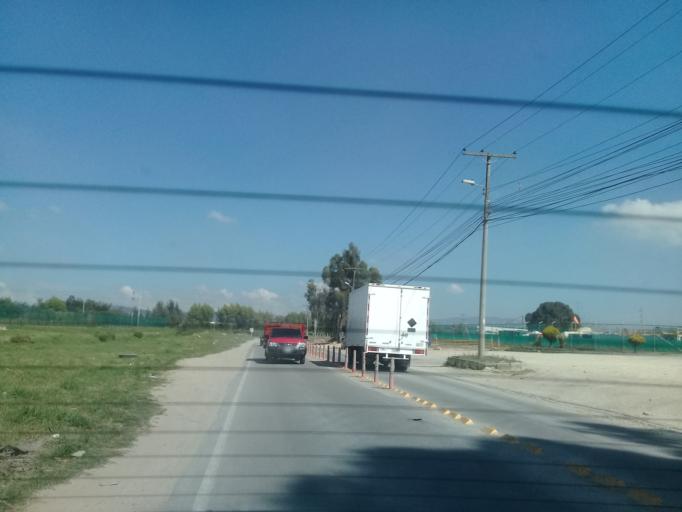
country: CO
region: Cundinamarca
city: Funza
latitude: 4.7474
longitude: -74.1635
